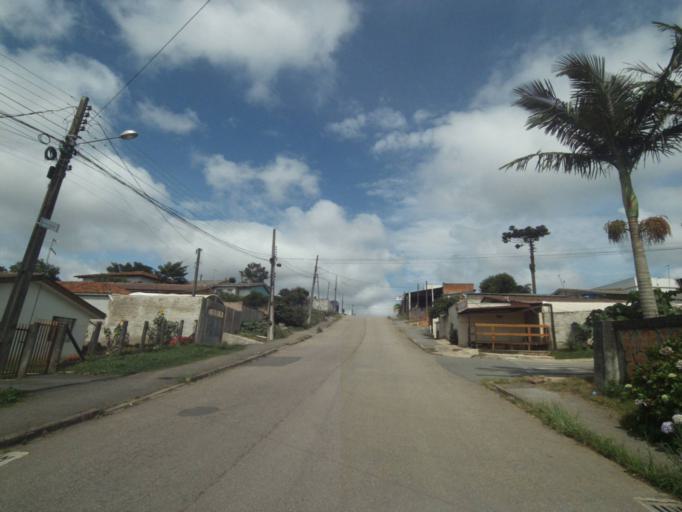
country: BR
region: Parana
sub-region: Quatro Barras
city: Quatro Barras
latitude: -25.3339
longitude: -49.0777
